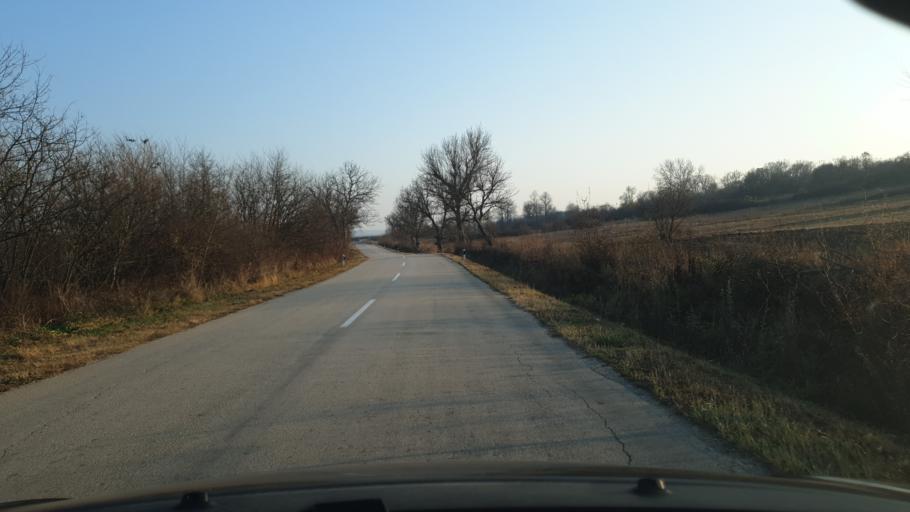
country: RS
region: Central Serbia
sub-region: Zajecarski Okrug
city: Zajecar
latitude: 43.9839
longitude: 22.2875
